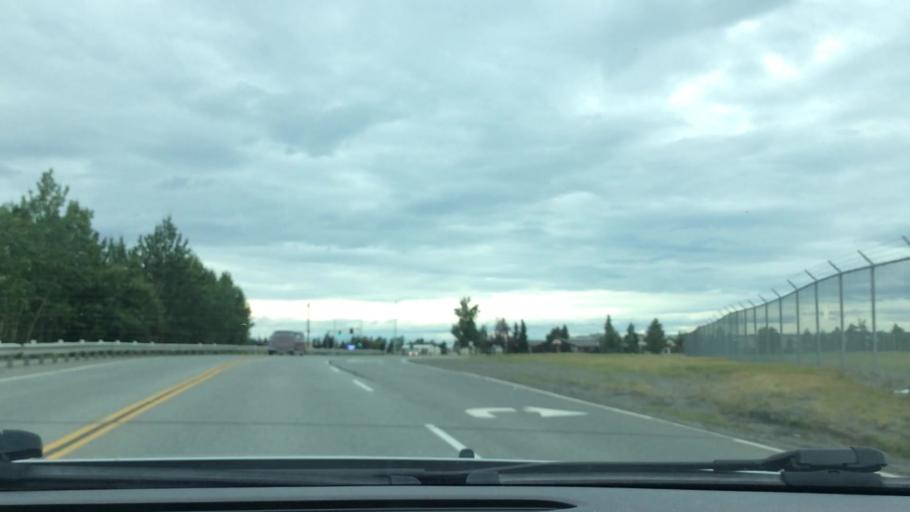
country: US
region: Alaska
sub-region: Anchorage Municipality
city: Anchorage
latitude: 61.2394
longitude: -149.7965
